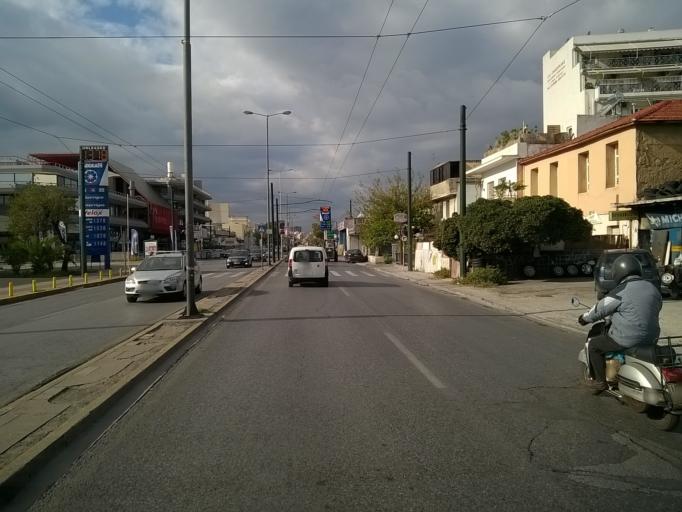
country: GR
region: Attica
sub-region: Nomos Piraios
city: Agios Ioannis Rentis
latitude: 37.9525
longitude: 23.6667
